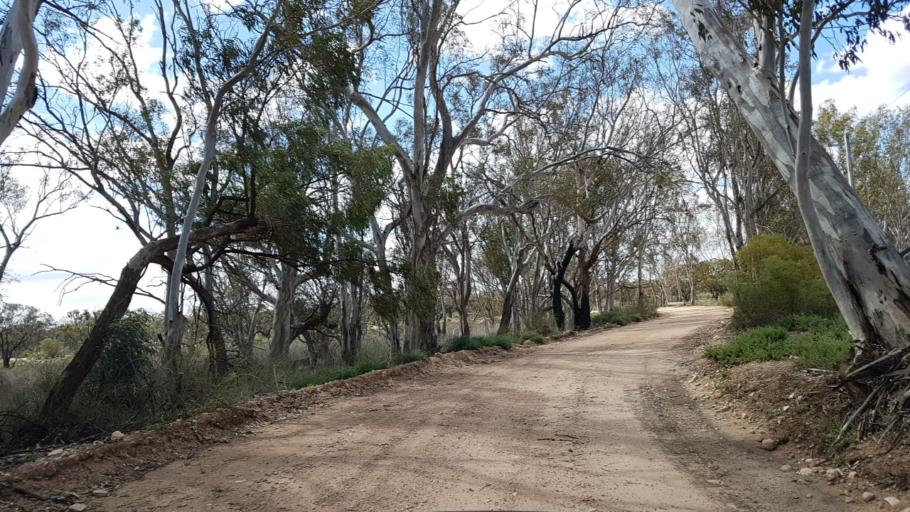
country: AU
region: South Australia
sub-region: Loxton Waikerie
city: Waikerie
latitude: -34.1653
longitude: 140.0237
